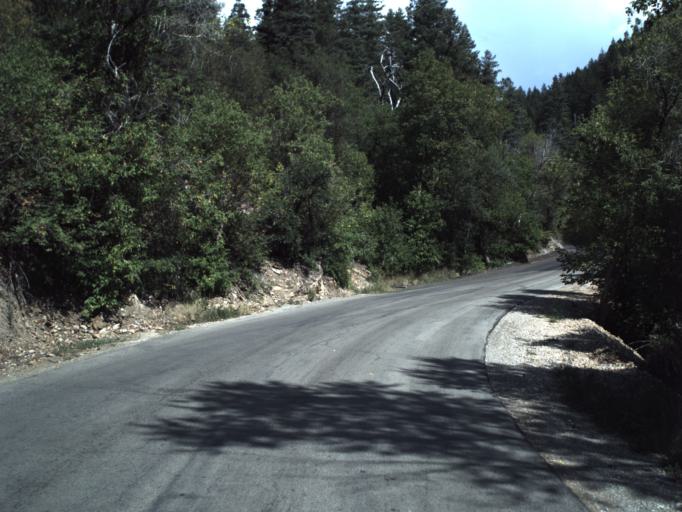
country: US
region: Utah
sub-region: Utah County
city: Cedar Hills
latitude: 40.4623
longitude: -111.6577
